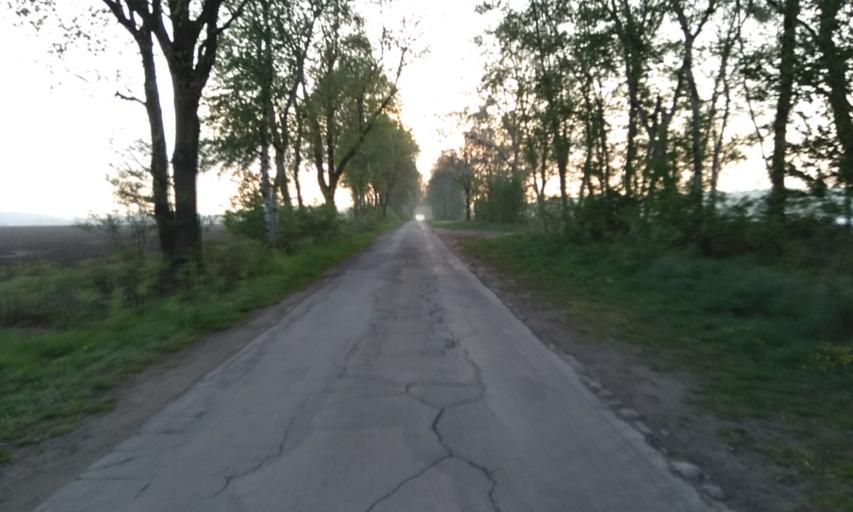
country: DE
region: Lower Saxony
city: Deinste
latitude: 53.4979
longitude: 9.4297
